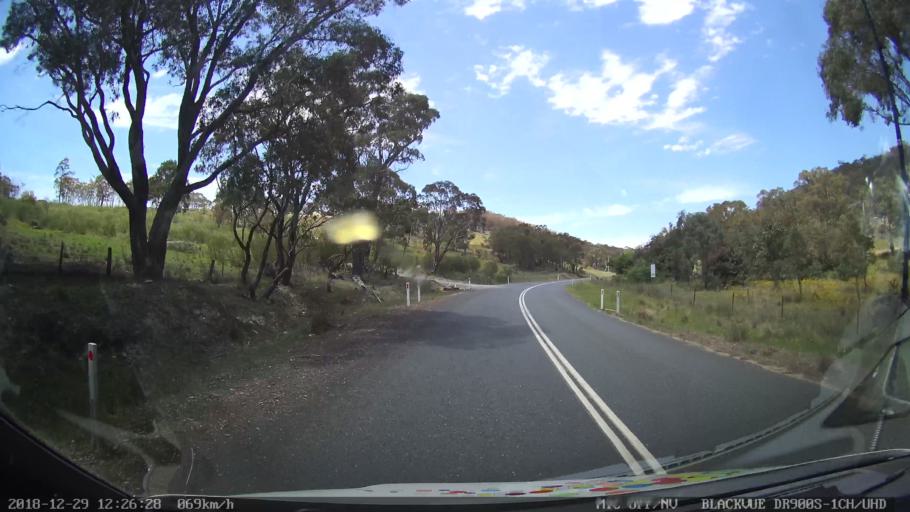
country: AU
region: New South Wales
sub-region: Queanbeyan
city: Queanbeyan
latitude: -35.4656
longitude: 149.2238
